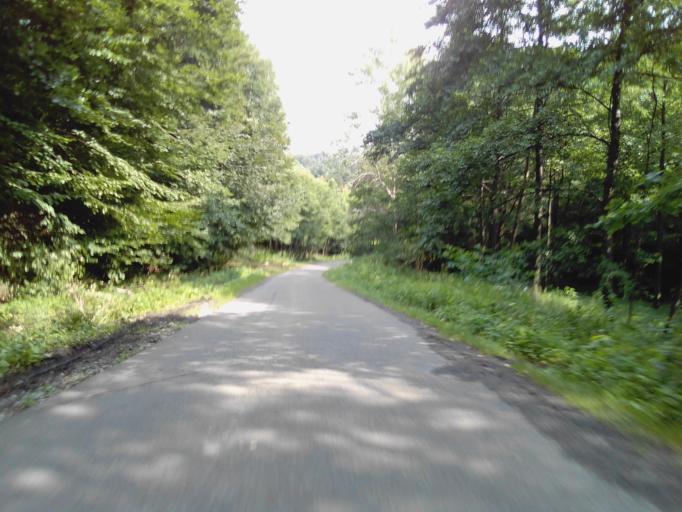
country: PL
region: Subcarpathian Voivodeship
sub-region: Powiat strzyzowski
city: Frysztak
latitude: 49.8623
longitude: 21.5438
